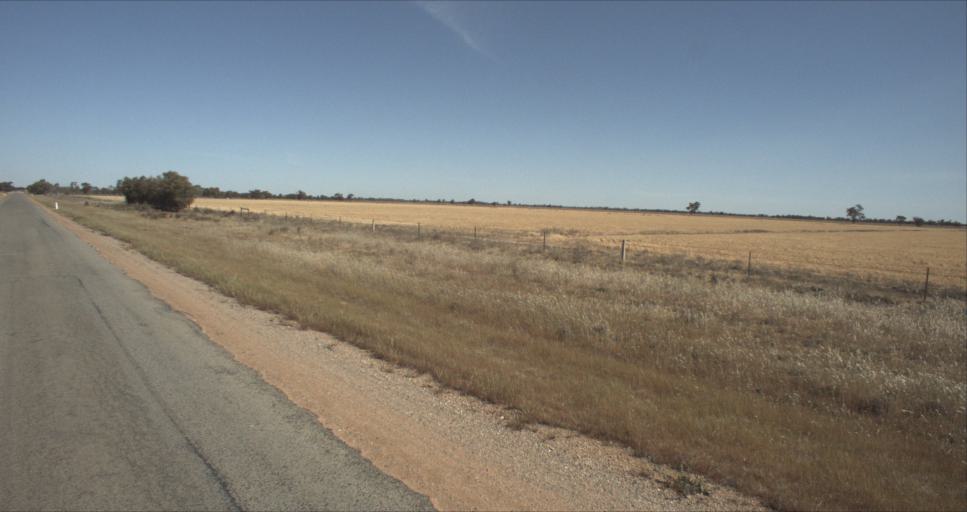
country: AU
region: New South Wales
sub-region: Leeton
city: Leeton
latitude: -34.4940
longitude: 146.3869
